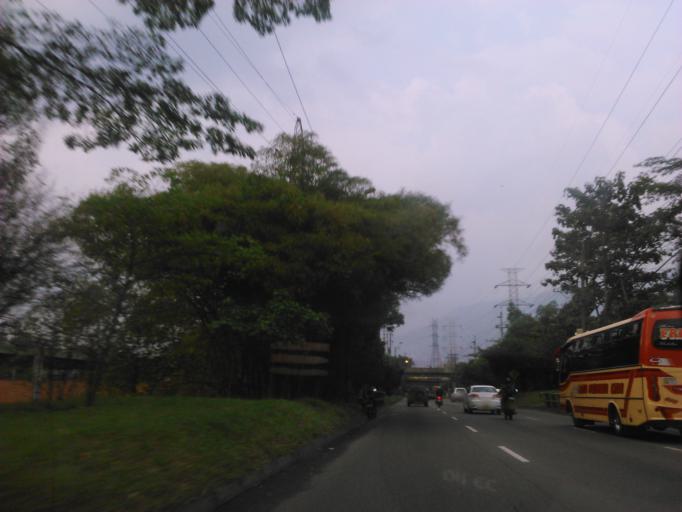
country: CO
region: Antioquia
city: Envigado
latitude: 6.1739
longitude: -75.5974
